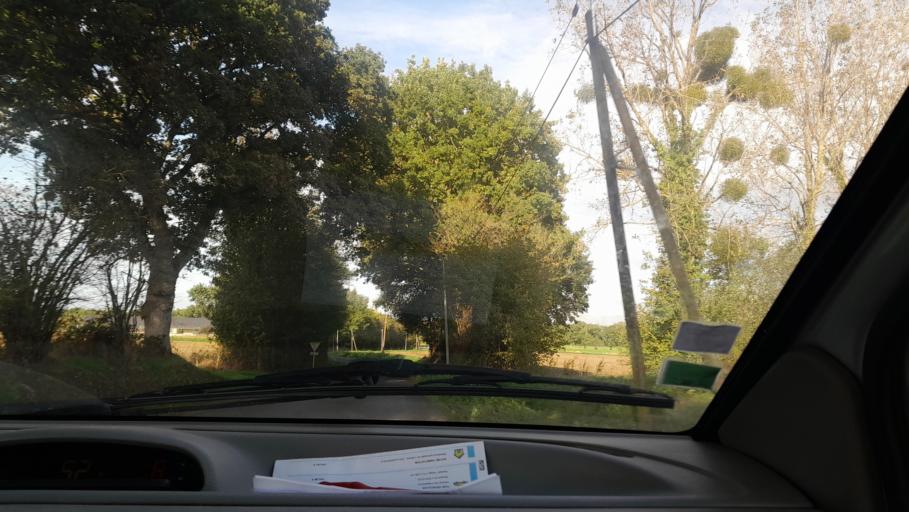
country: FR
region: Lower Normandy
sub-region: Departement de la Manche
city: Pontorson
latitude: 48.5563
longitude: -1.4568
